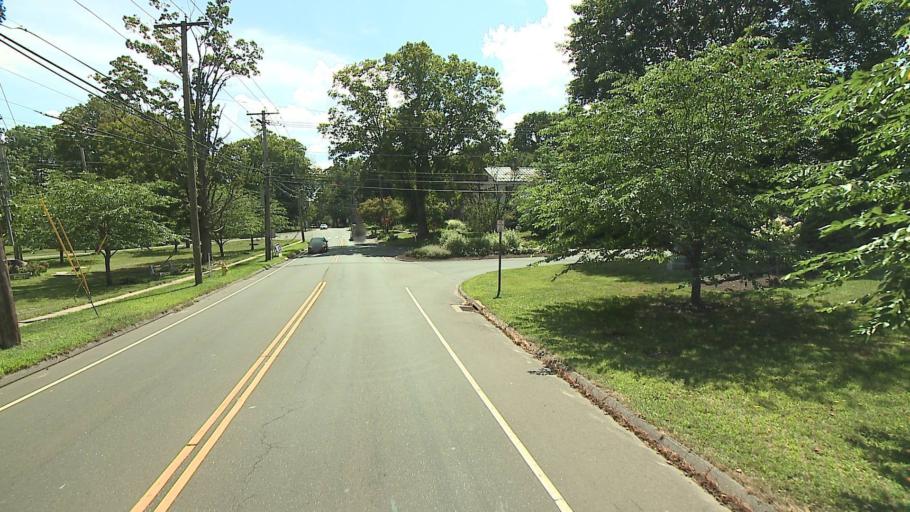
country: US
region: Connecticut
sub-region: Fairfield County
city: Trumbull
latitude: 41.2417
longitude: -73.1619
